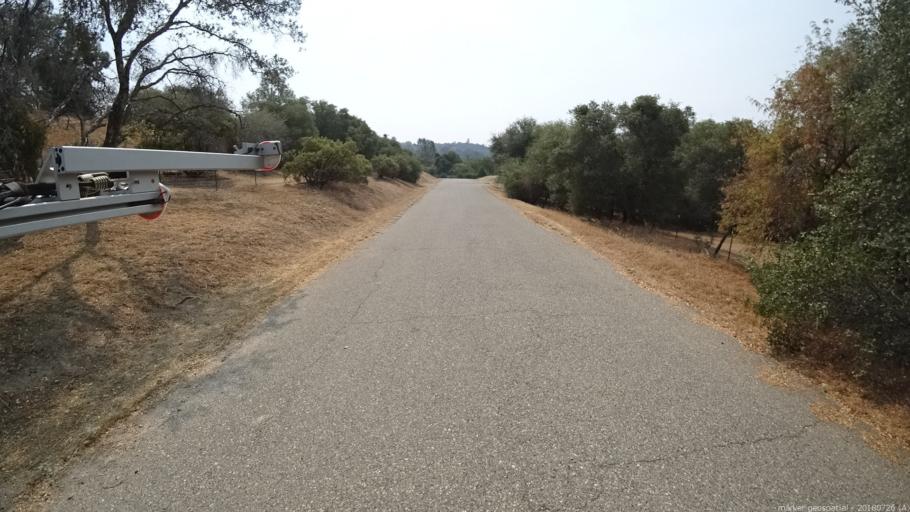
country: US
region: California
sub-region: Madera County
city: Coarsegold
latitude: 37.2447
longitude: -119.7044
